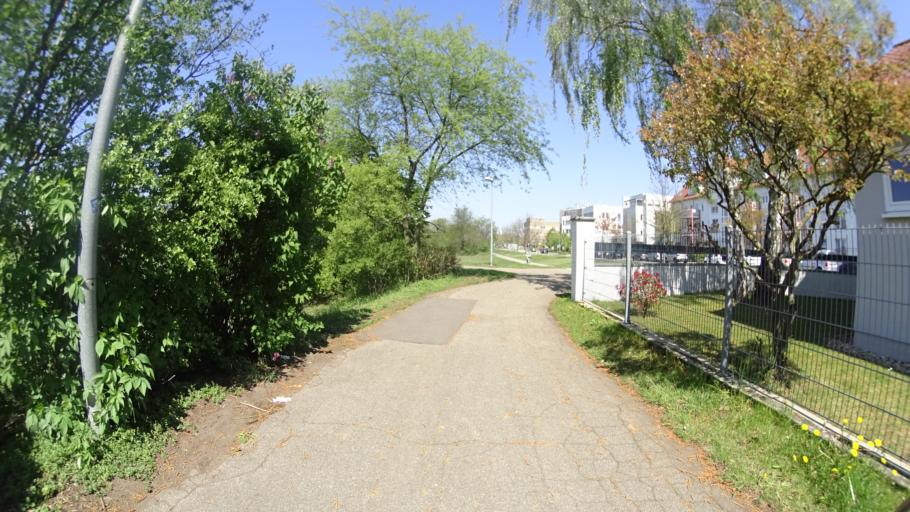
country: DE
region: Baden-Wuerttemberg
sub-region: Karlsruhe Region
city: Karlsruhe
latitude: 49.0429
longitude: 8.3891
